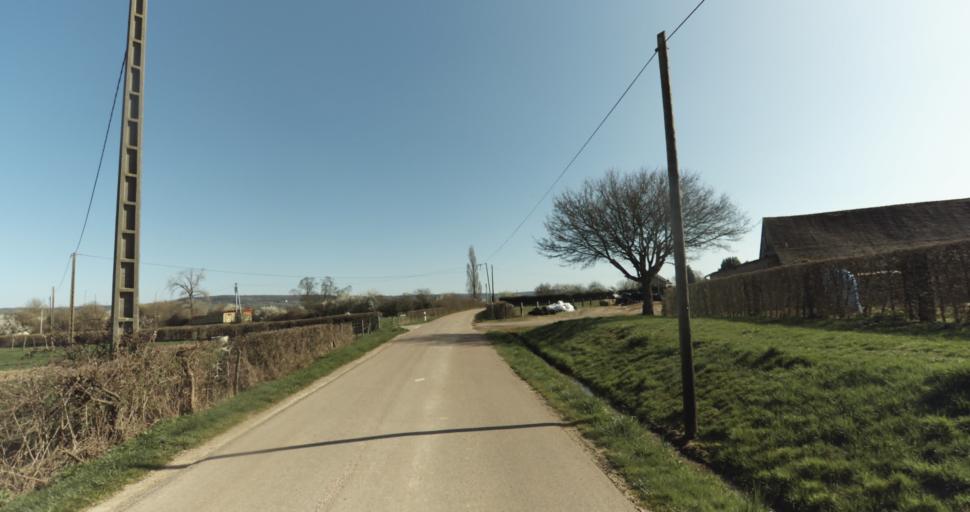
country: FR
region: Lower Normandy
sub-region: Departement du Calvados
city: Saint-Pierre-sur-Dives
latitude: 48.9576
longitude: 0.0074
